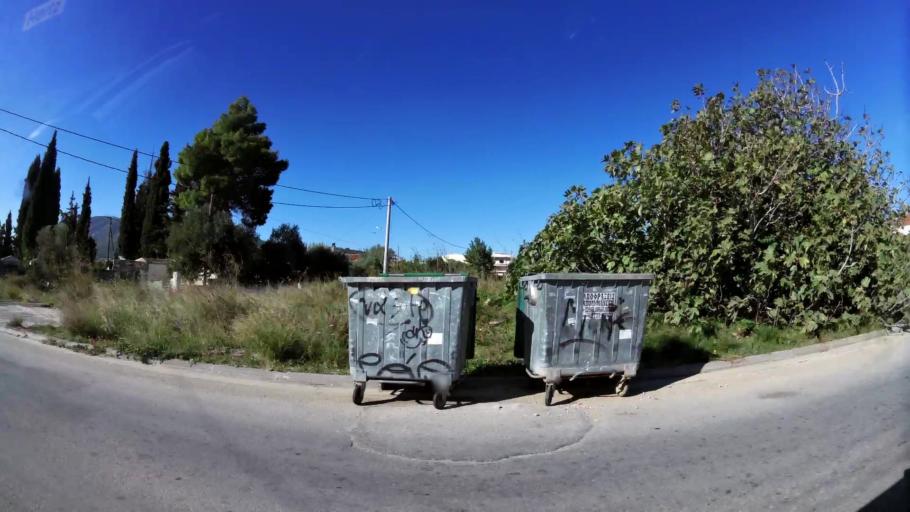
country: GR
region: Attica
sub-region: Nomarchia Anatolikis Attikis
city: Gerakas
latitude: 38.0140
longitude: 23.8623
